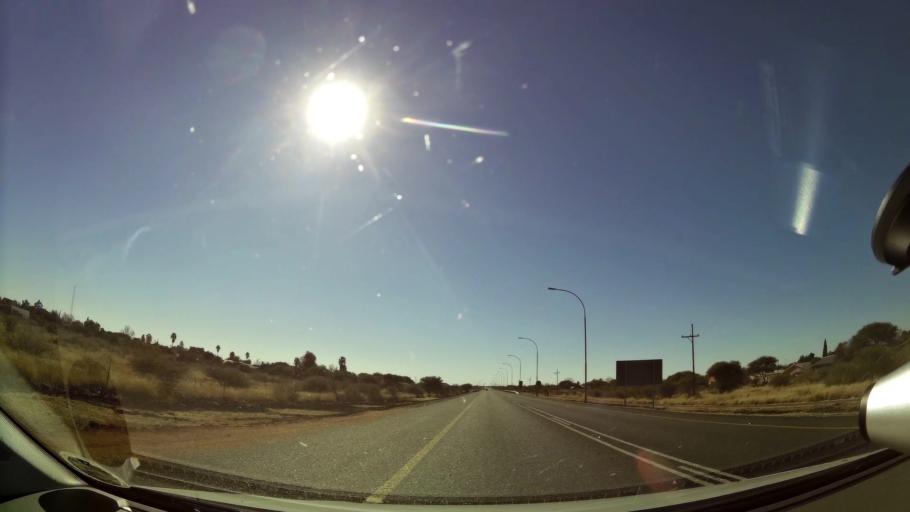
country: ZA
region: Northern Cape
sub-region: Frances Baard District Municipality
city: Warrenton
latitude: -28.1113
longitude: 24.8558
